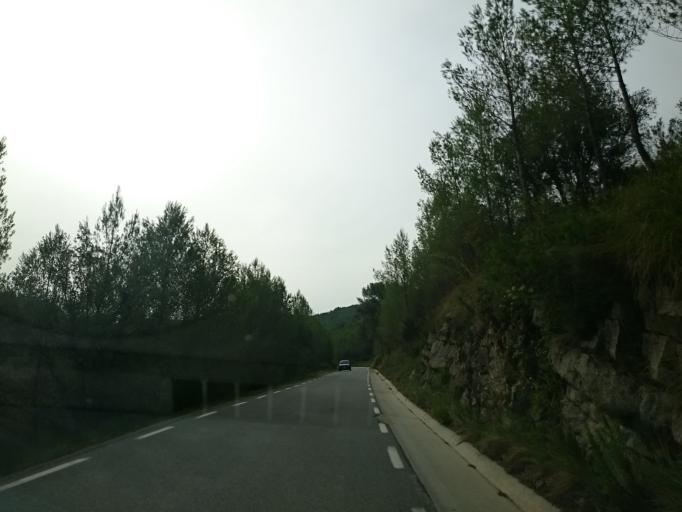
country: ES
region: Catalonia
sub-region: Provincia de Barcelona
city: Olivella
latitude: 41.3108
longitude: 1.7964
